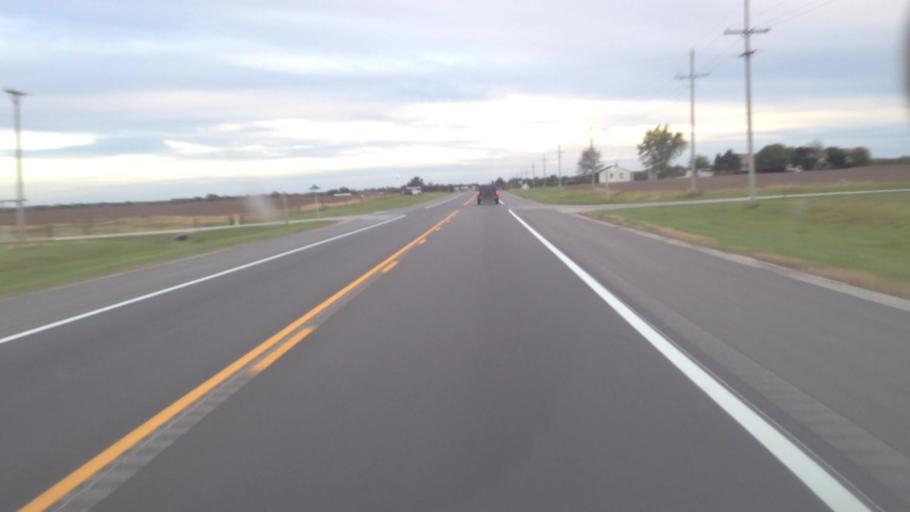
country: US
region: Kansas
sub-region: Franklin County
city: Ottawa
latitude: 38.5073
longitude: -95.2675
